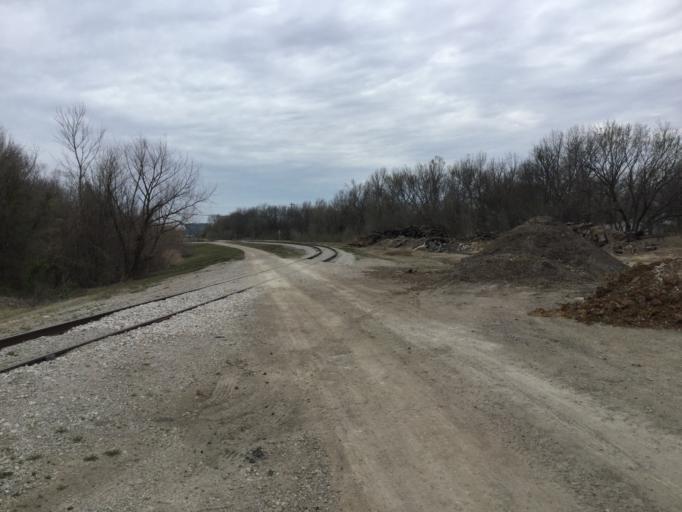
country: US
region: Kansas
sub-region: Wilson County
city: Fredonia
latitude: 37.5413
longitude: -95.8297
